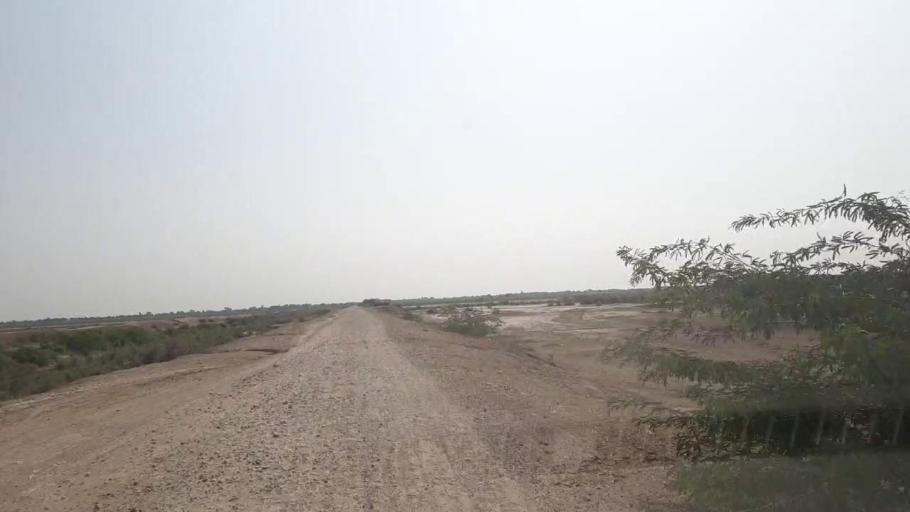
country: PK
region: Sindh
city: Kadhan
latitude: 24.4758
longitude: 68.9025
